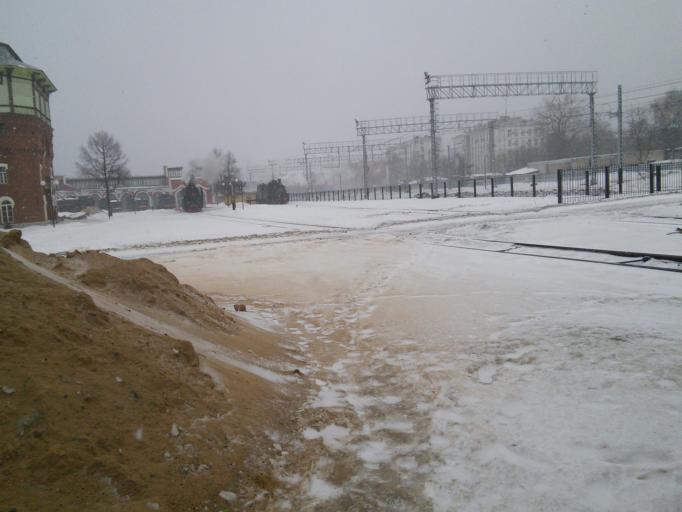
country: RU
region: Moskovskaya
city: Koptevo
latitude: 55.8140
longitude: 37.5272
